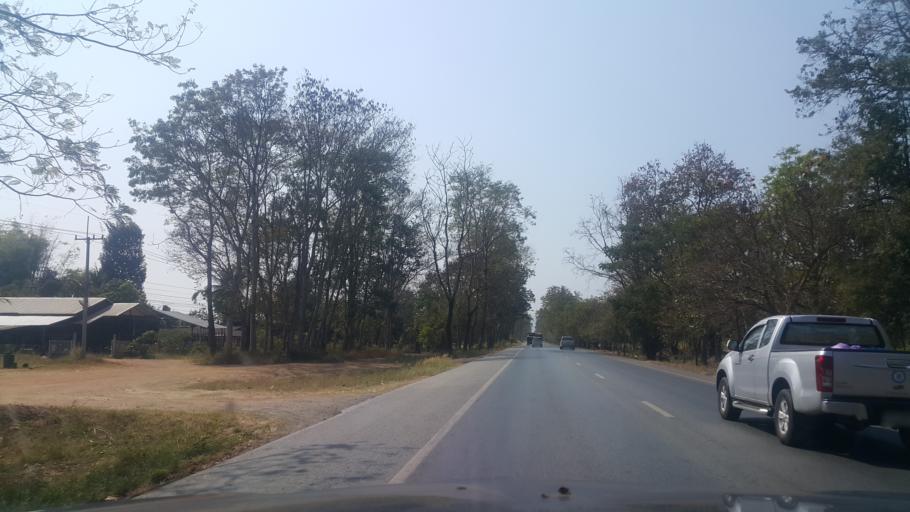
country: TH
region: Nakhon Ratchasima
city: Wang Nam Khiao
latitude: 14.5501
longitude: 101.9729
